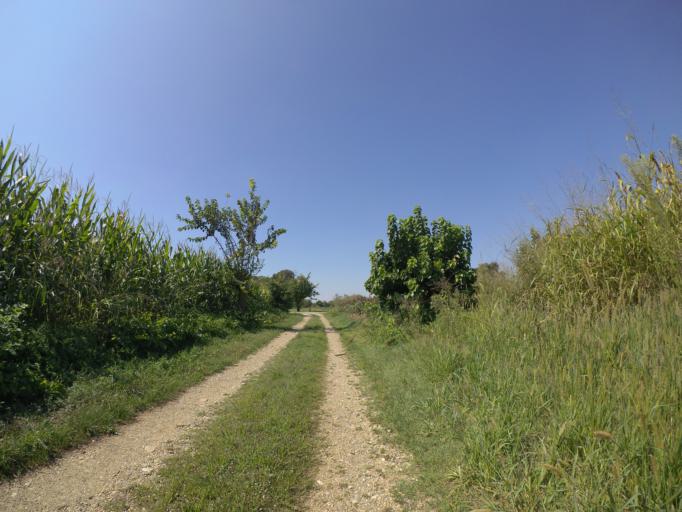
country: IT
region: Friuli Venezia Giulia
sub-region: Provincia di Udine
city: Talmassons
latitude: 45.9399
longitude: 13.0907
